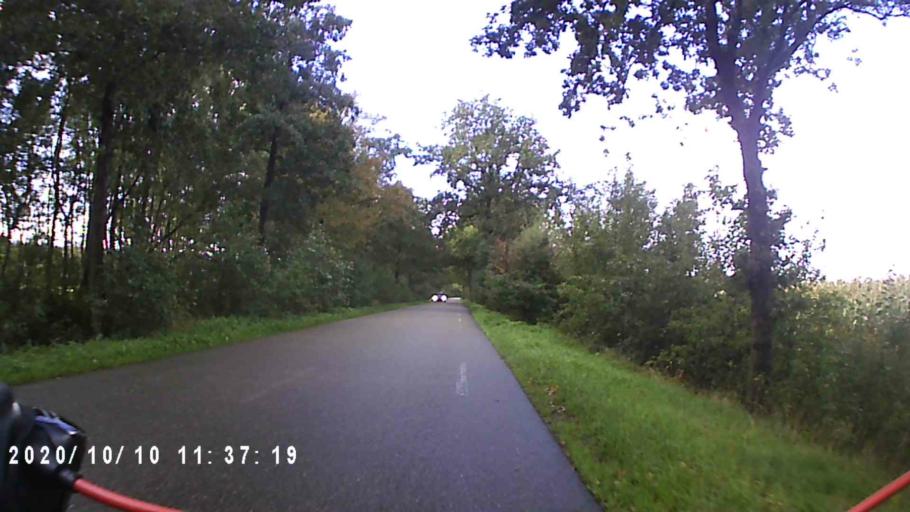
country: NL
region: Friesland
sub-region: Gemeente Smallingerland
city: Drachten
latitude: 53.0735
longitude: 6.1148
